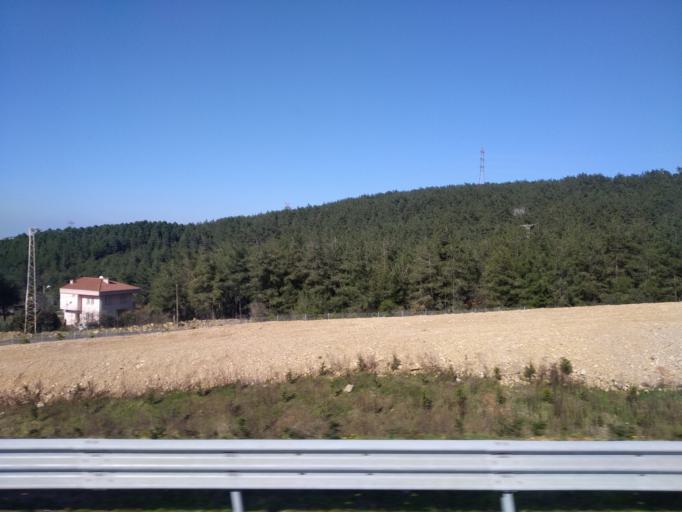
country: TR
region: Istanbul
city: Umraniye
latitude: 41.0509
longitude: 29.1596
